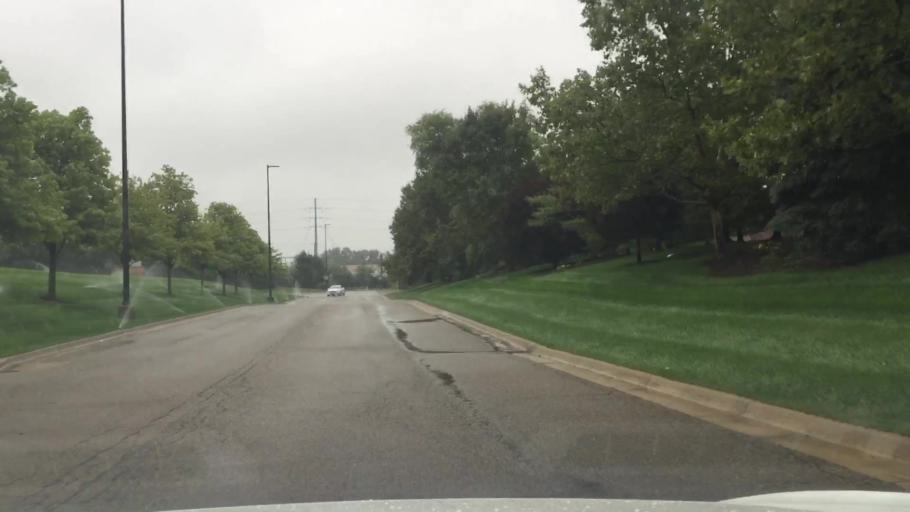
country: US
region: Michigan
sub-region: Wayne County
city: Livonia
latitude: 42.3793
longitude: -83.3266
